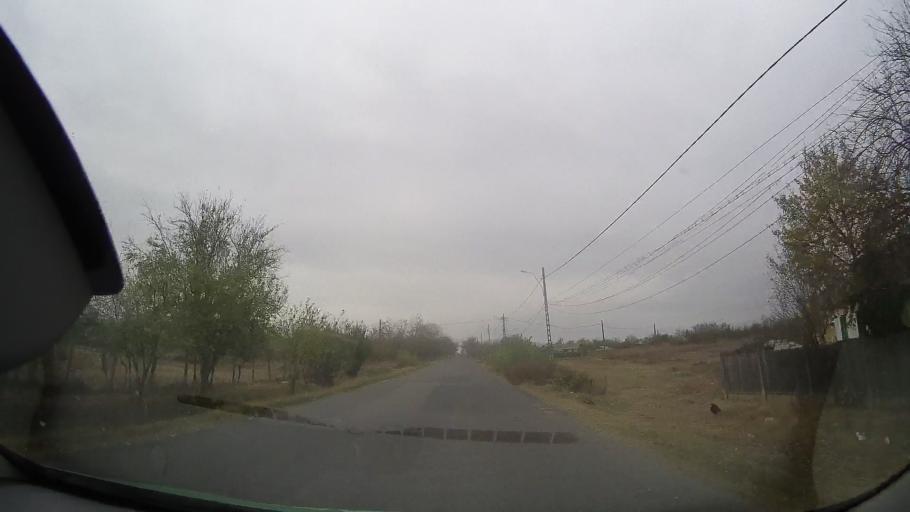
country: RO
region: Braila
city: Dudesti
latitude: 44.9428
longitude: 27.4193
